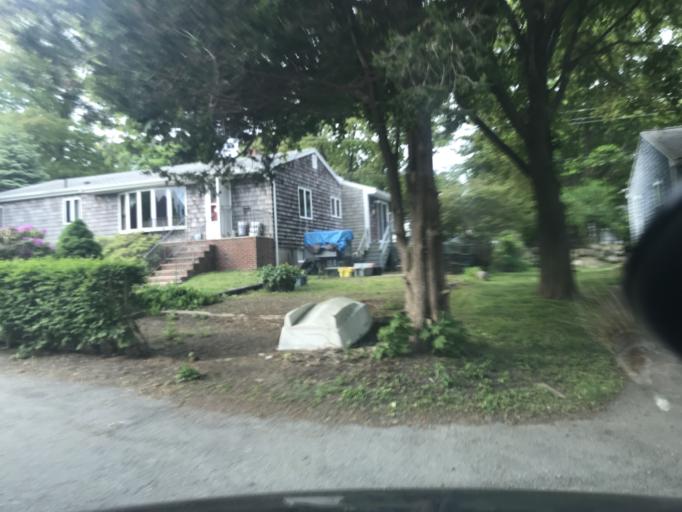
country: US
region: Massachusetts
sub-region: Essex County
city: Rockport
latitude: 42.6523
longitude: -70.6267
